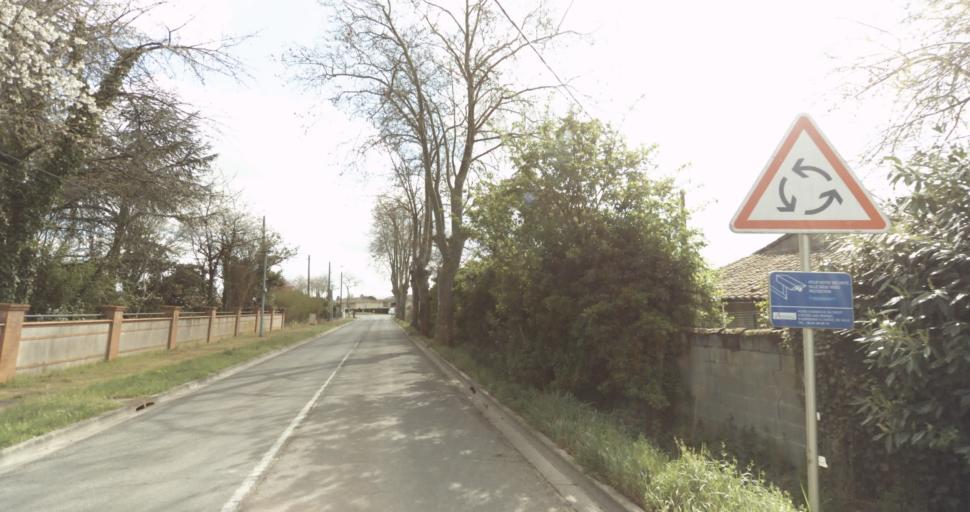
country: FR
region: Midi-Pyrenees
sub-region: Departement de la Haute-Garonne
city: Auterive
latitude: 43.3589
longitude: 1.4765
